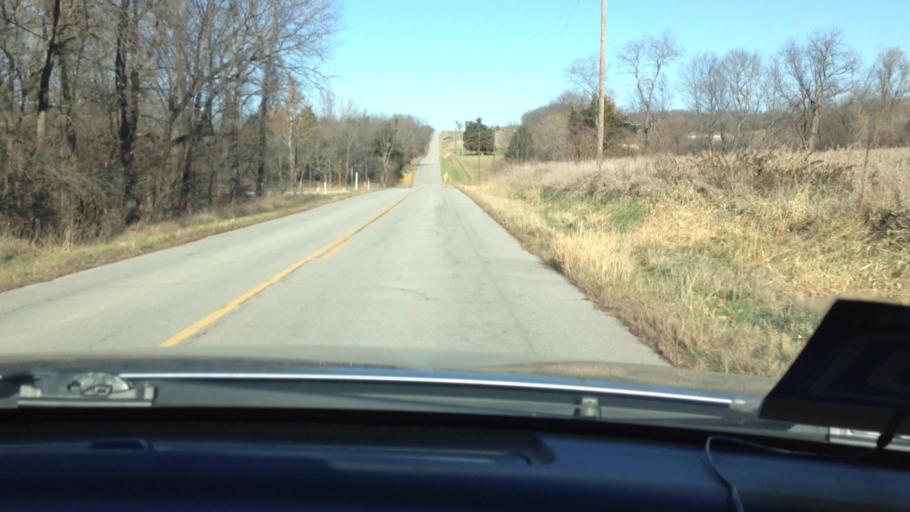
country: US
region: Missouri
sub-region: Platte County
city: Weston
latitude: 39.4671
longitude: -94.9007
